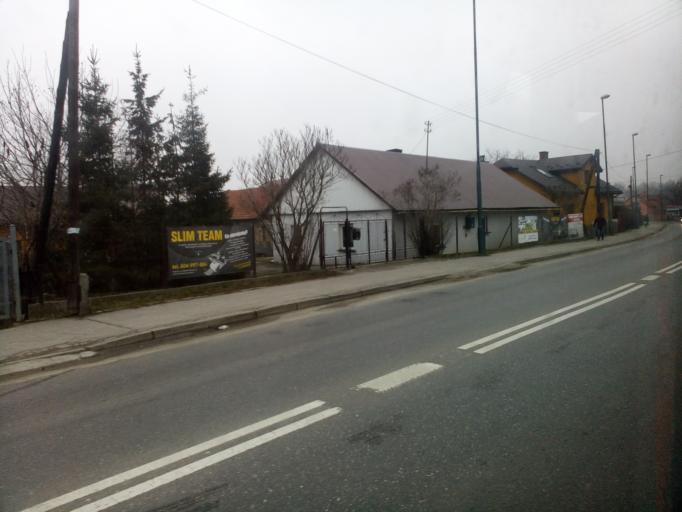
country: PL
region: Lesser Poland Voivodeship
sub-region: Powiat nowosadecki
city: Stary Sacz
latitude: 49.5792
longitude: 20.6661
